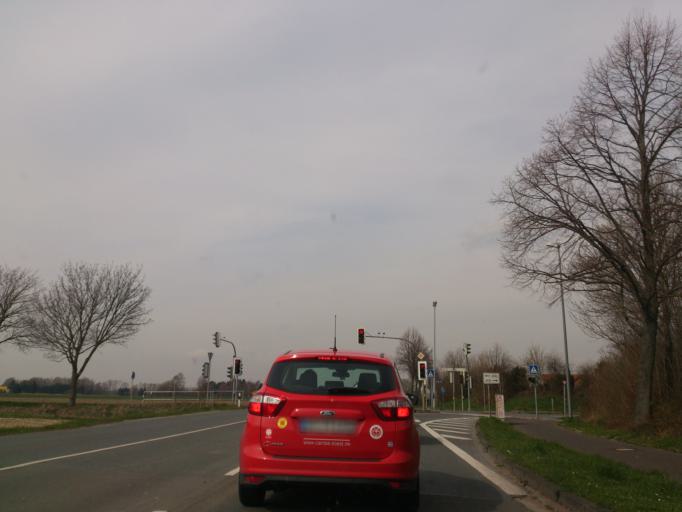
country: DE
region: North Rhine-Westphalia
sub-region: Regierungsbezirk Arnsberg
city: Soest
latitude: 51.5539
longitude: 8.0922
